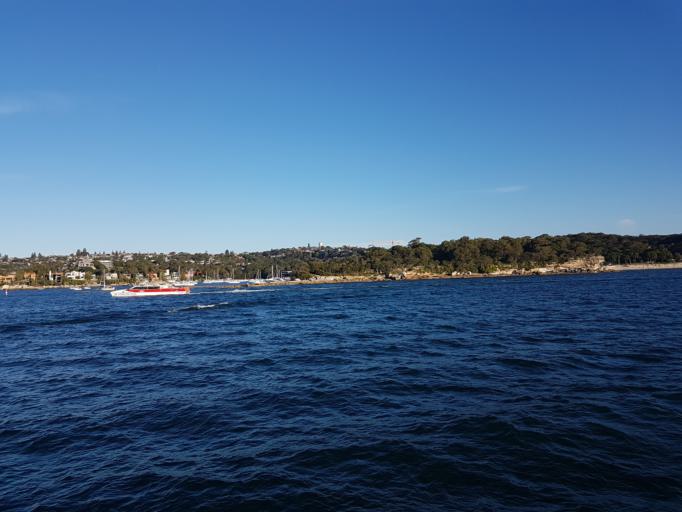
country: AU
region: New South Wales
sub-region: Waverley
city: Dover Heights
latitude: -33.8452
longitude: 151.2687
